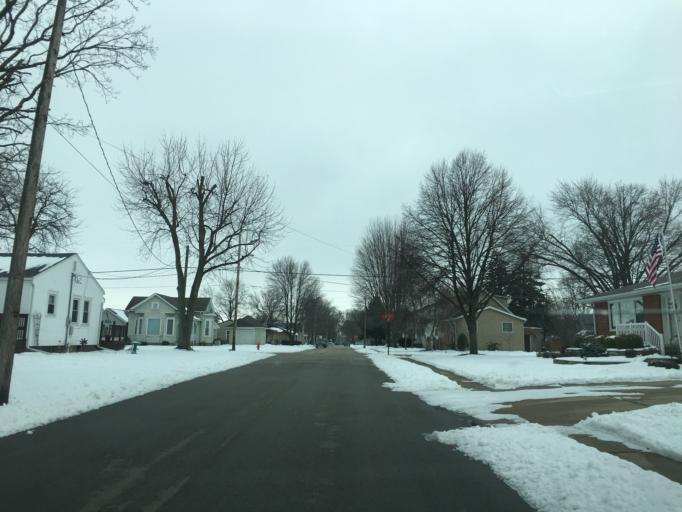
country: US
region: Illinois
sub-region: LaSalle County
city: Peru
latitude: 41.3326
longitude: -89.1306
